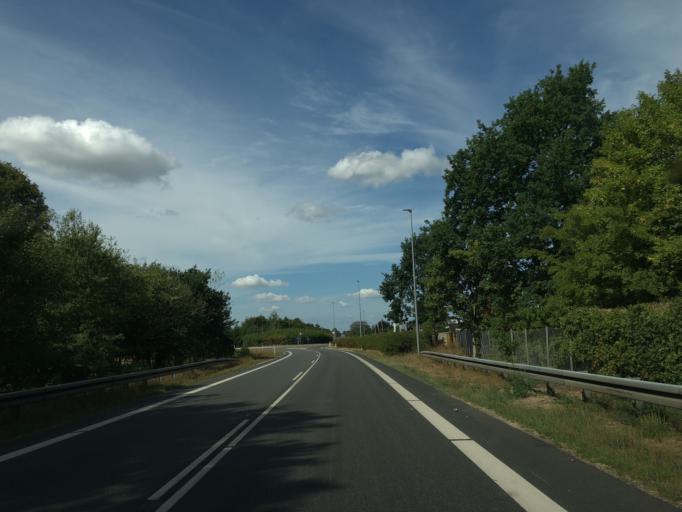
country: DK
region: Central Jutland
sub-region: Ikast-Brande Kommune
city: Bording Kirkeby
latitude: 56.1406
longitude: 9.2763
